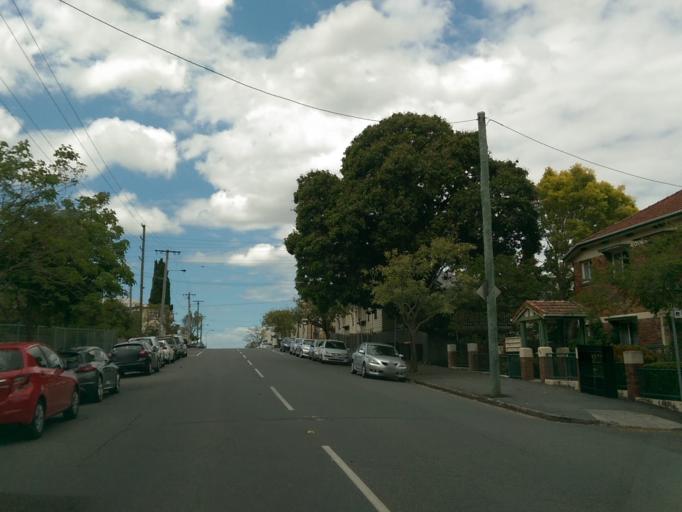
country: AU
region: Queensland
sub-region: Brisbane
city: Fortitude Valley
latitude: -27.4659
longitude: 153.0412
